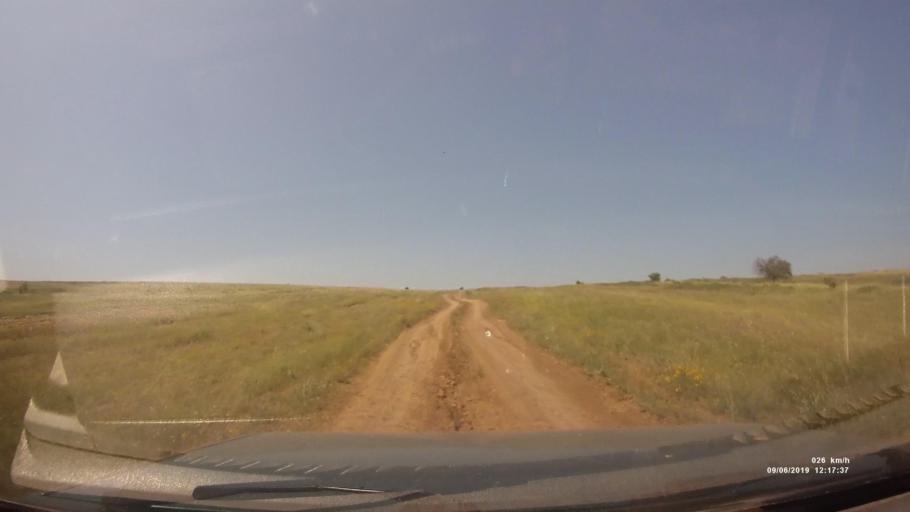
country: RU
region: Rostov
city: Staraya Stanitsa
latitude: 48.2556
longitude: 40.3143
